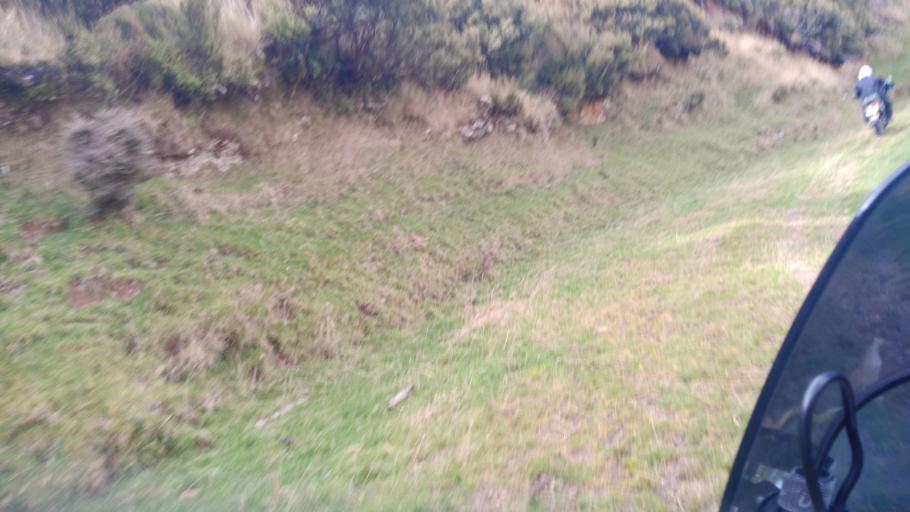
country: NZ
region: Gisborne
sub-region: Gisborne District
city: Gisborne
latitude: -38.4764
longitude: 177.5342
